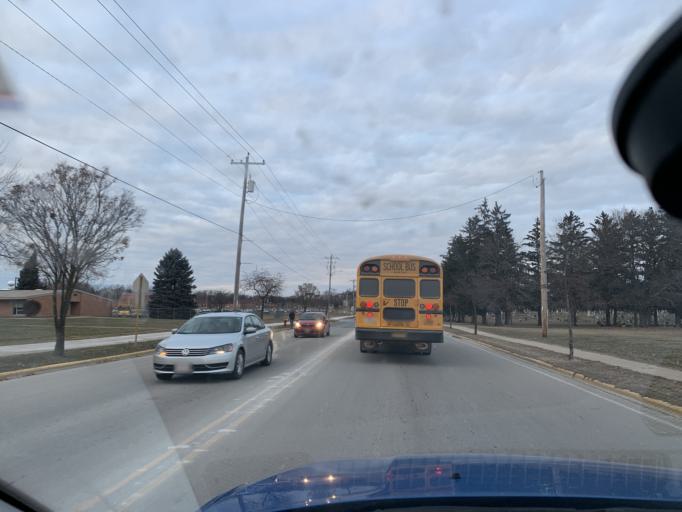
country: US
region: Wisconsin
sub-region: Dane County
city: Verona
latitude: 42.9956
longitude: -89.5335
